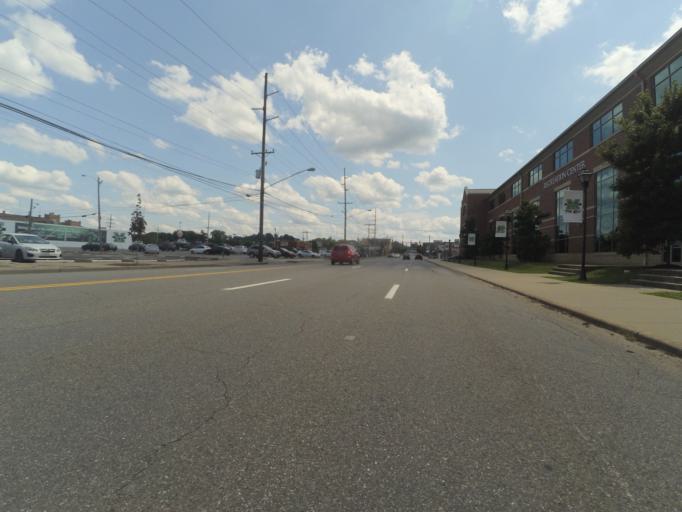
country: US
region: West Virginia
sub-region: Cabell County
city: Huntington
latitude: 38.4239
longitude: -82.4228
